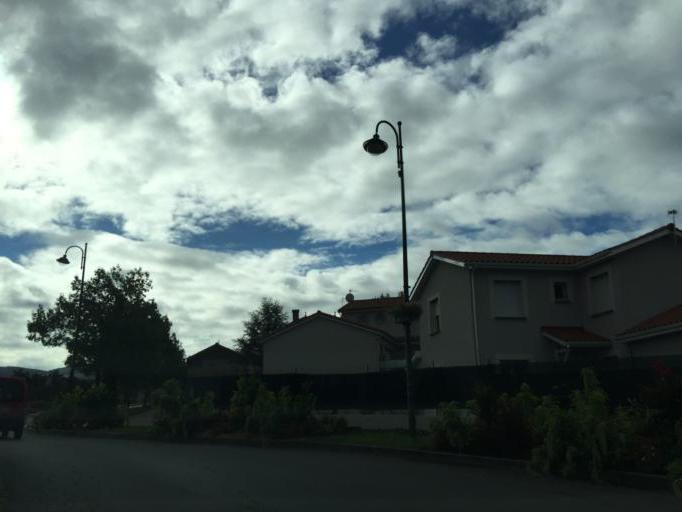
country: FR
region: Rhone-Alpes
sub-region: Departement de la Loire
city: Saint-Paul-en-Jarez
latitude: 45.4928
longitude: 4.5674
